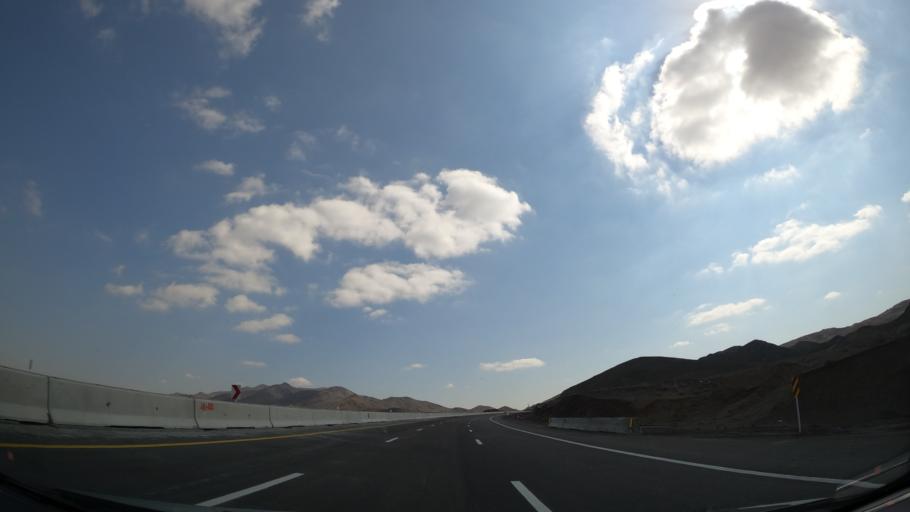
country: IR
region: Alborz
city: Nazarabad
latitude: 35.6946
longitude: 50.6317
